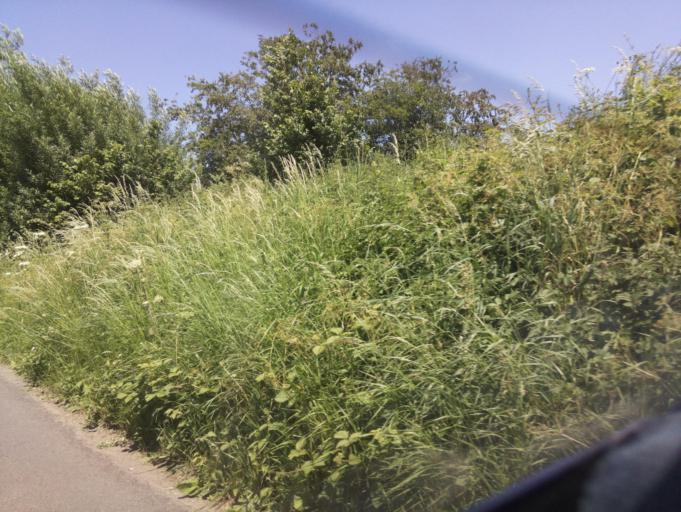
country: GB
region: England
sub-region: Wiltshire
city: Bremhill
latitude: 51.5056
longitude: -2.0521
